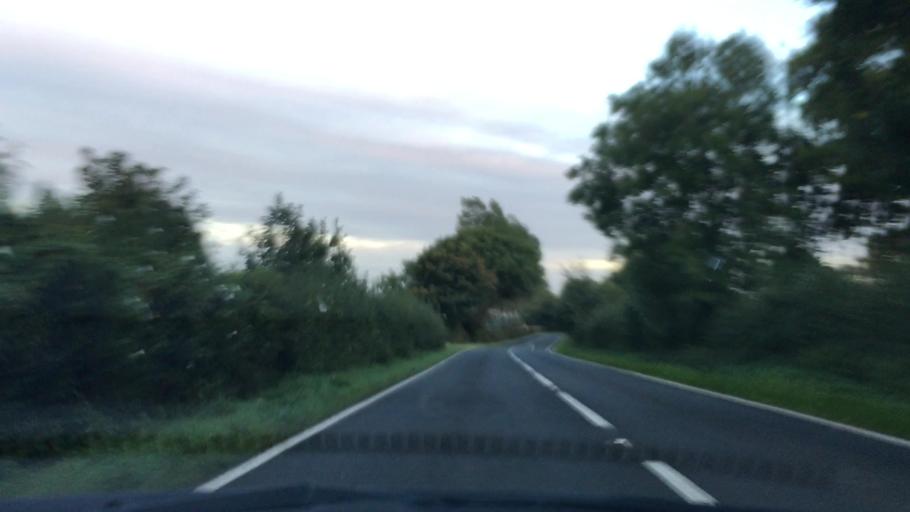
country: GB
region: England
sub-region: North East Lincolnshire
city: Wold Newton
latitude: 53.4629
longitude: -0.0981
